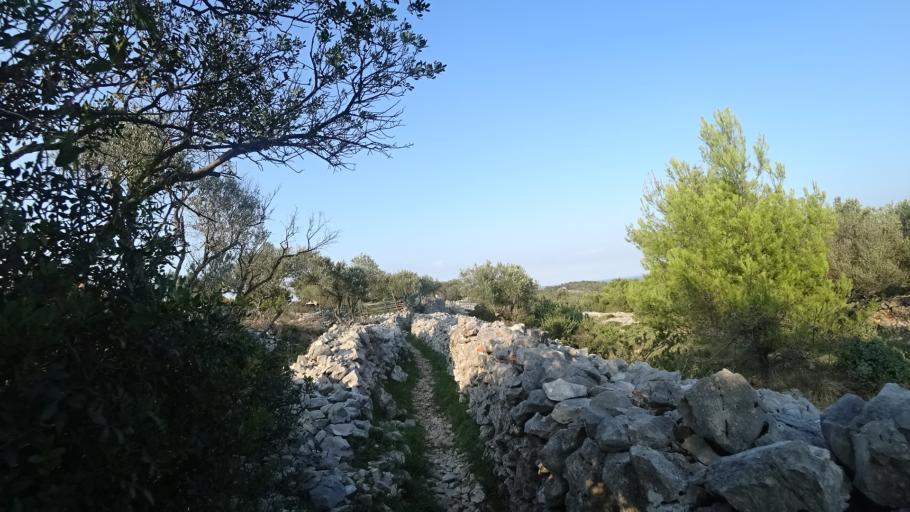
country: HR
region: Primorsko-Goranska
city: Mali Losinj
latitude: 44.5254
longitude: 14.4757
